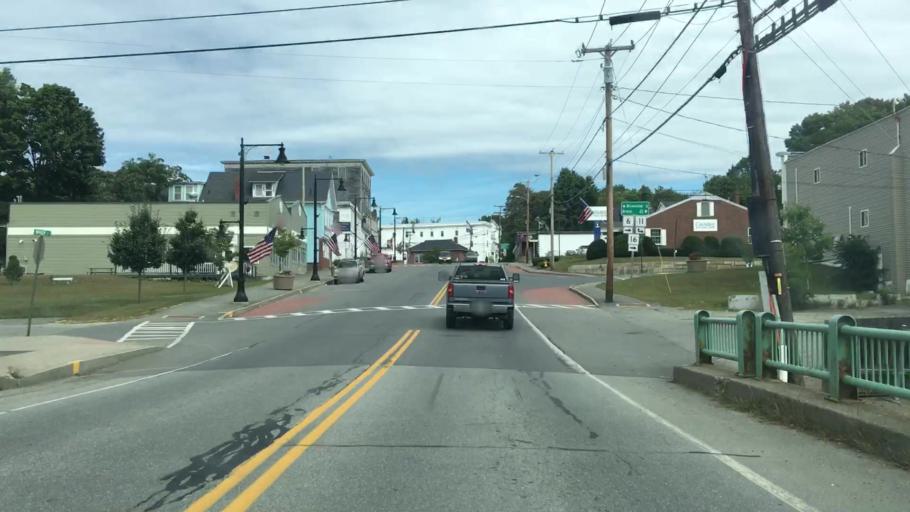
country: US
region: Maine
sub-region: Piscataquis County
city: Milo
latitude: 45.2517
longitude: -68.9870
